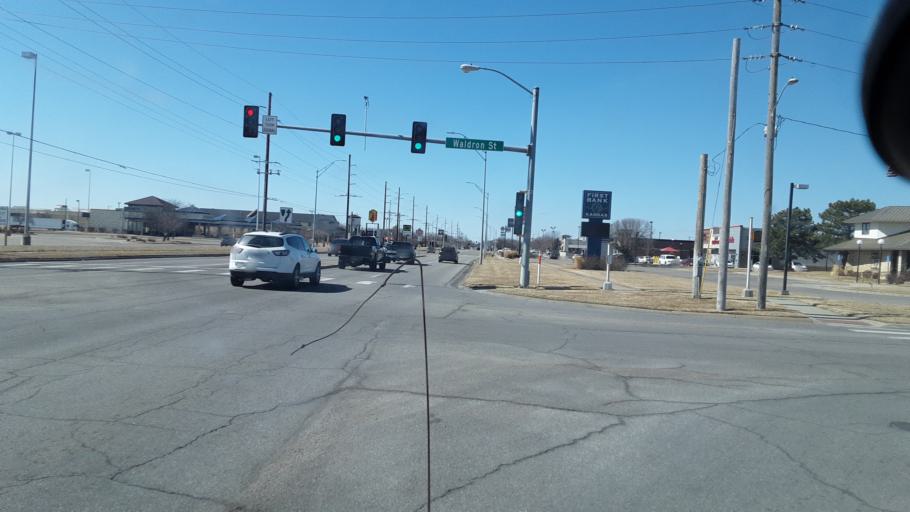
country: US
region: Kansas
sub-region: Reno County
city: Hutchinson
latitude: 38.0723
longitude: -97.8976
